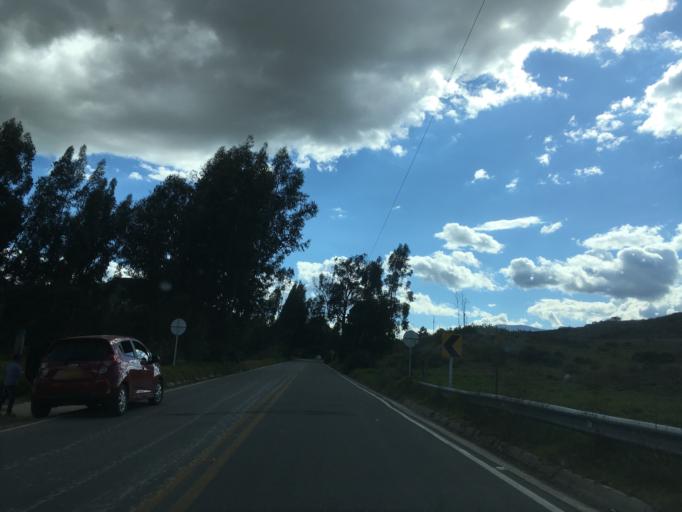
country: CO
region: Boyaca
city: Firavitoba
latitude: 5.6307
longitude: -73.0057
